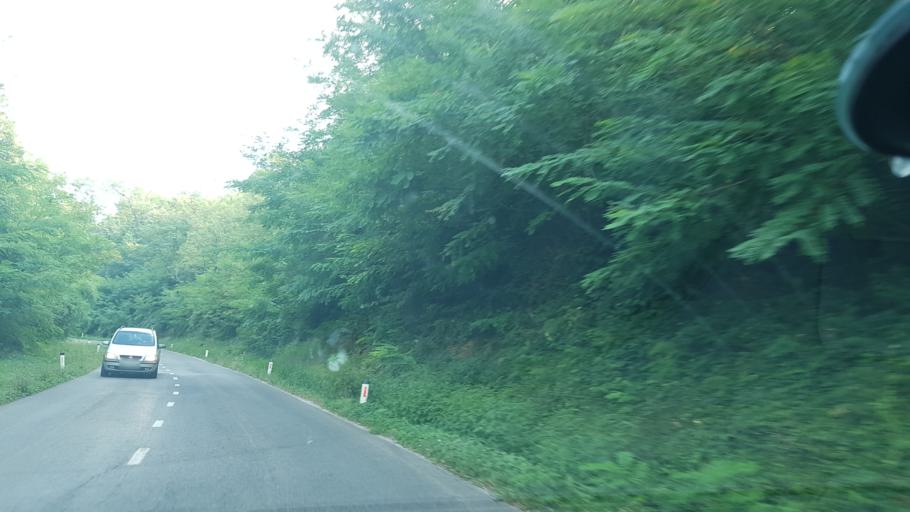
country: SI
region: Nova Gorica
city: Nova Gorica
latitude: 45.9487
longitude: 13.6429
